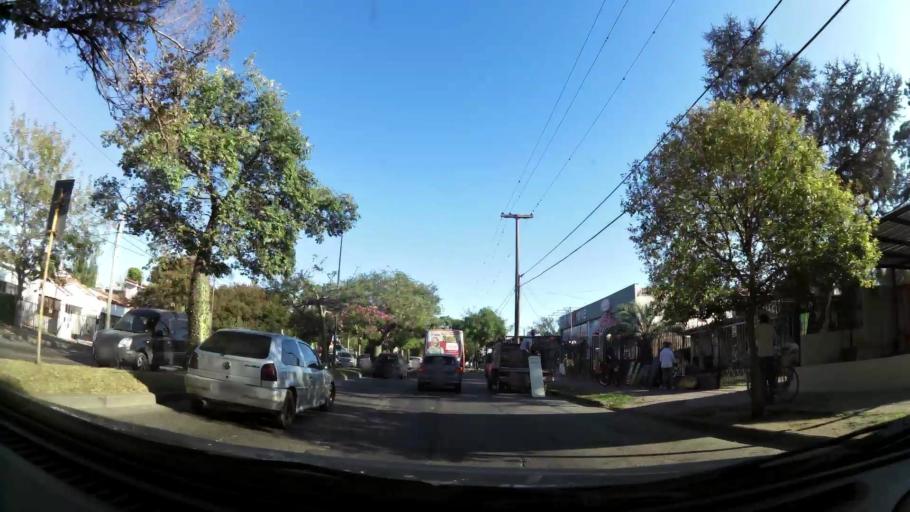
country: AR
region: Cordoba
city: Villa Allende
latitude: -31.3462
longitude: -64.2505
